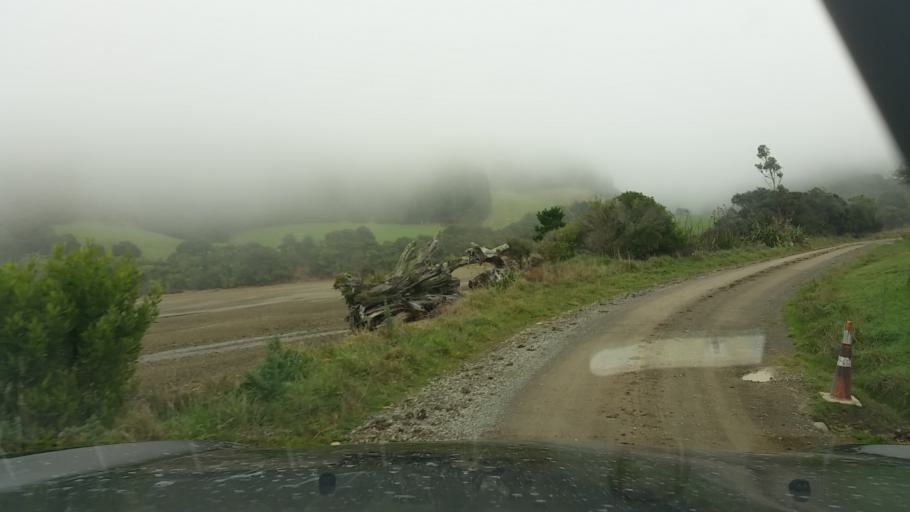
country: NZ
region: Marlborough
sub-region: Marlborough District
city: Picton
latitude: -41.1701
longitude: 174.0044
